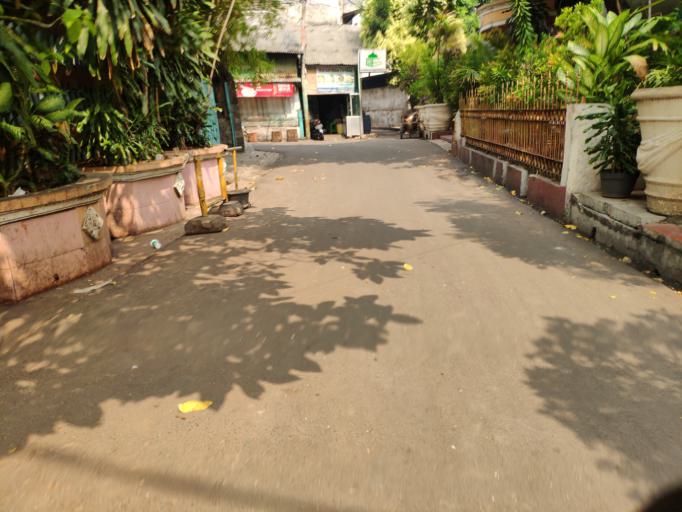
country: ID
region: Jakarta Raya
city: Jakarta
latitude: -6.1969
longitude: 106.8665
